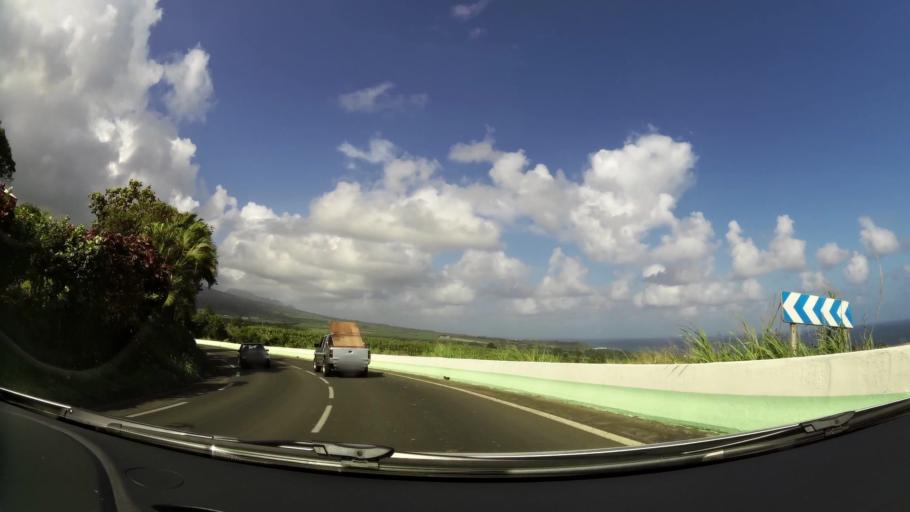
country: MQ
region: Martinique
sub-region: Martinique
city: Le Lorrain
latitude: 14.8365
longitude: -61.0740
